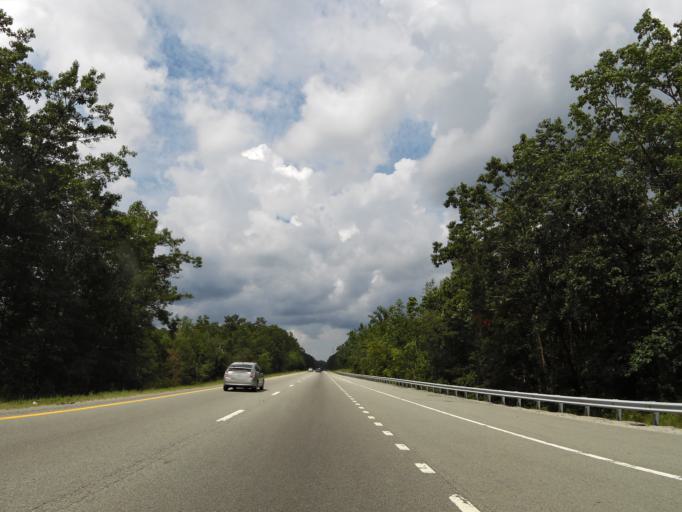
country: US
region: Tennessee
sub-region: Putnam County
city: Monterey
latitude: 36.0829
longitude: -85.2141
